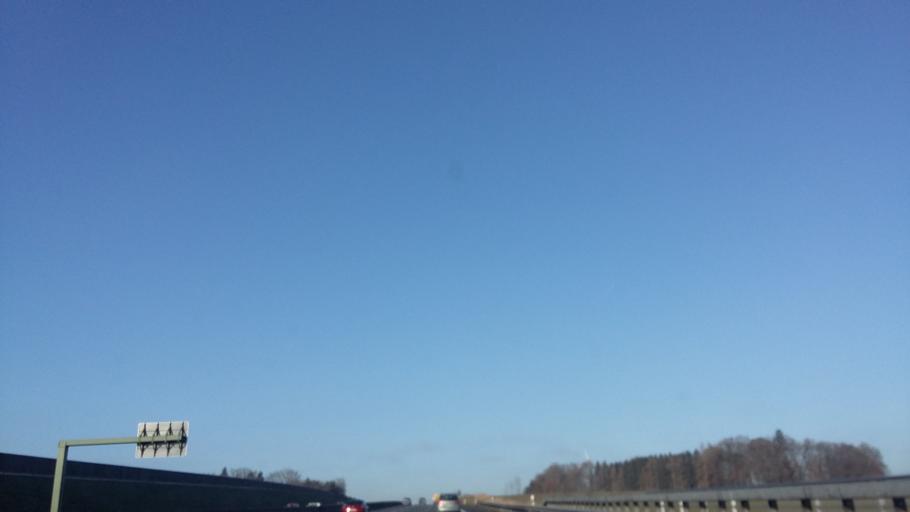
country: DE
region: Bavaria
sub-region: Upper Bavaria
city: Odelzhausen
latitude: 48.3166
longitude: 11.1945
